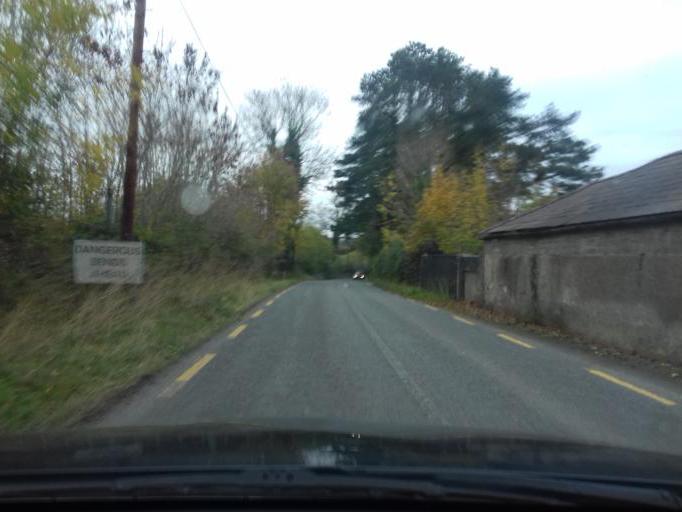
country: IE
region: Leinster
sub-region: Kildare
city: Maynooth
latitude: 53.3880
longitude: -6.5843
